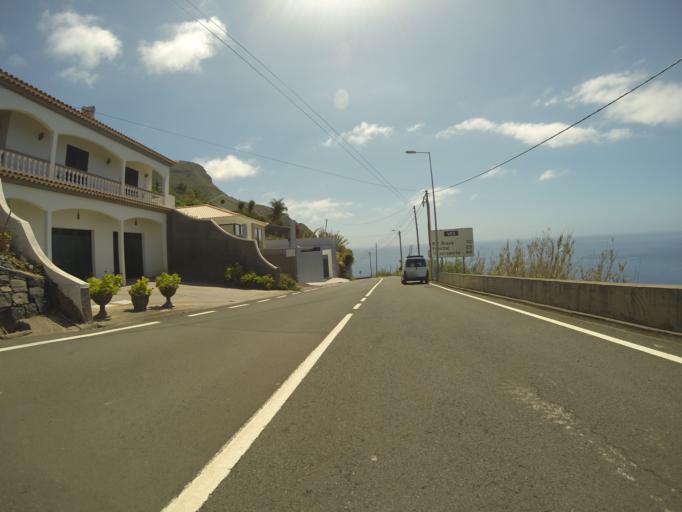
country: PT
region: Madeira
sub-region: Calheta
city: Arco da Calheta
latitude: 32.7090
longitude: -17.1487
